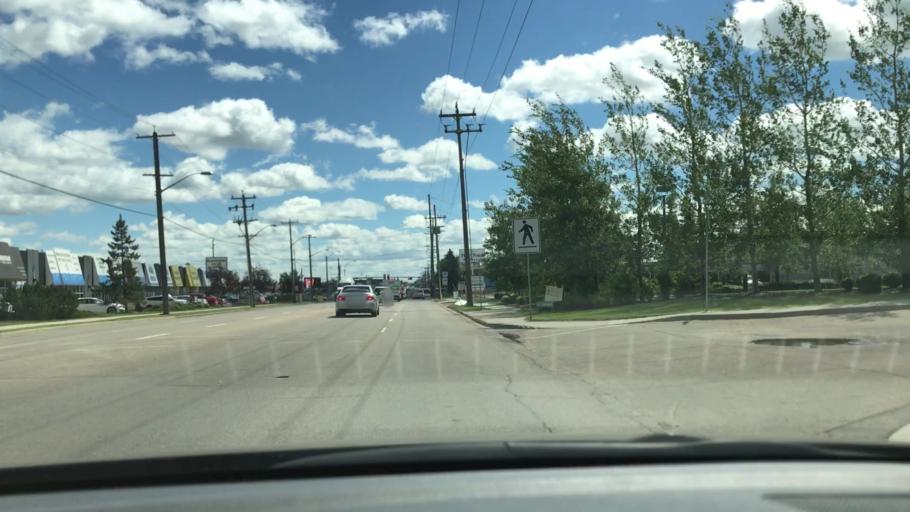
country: CA
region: Alberta
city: Edmonton
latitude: 53.4904
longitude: -113.4862
